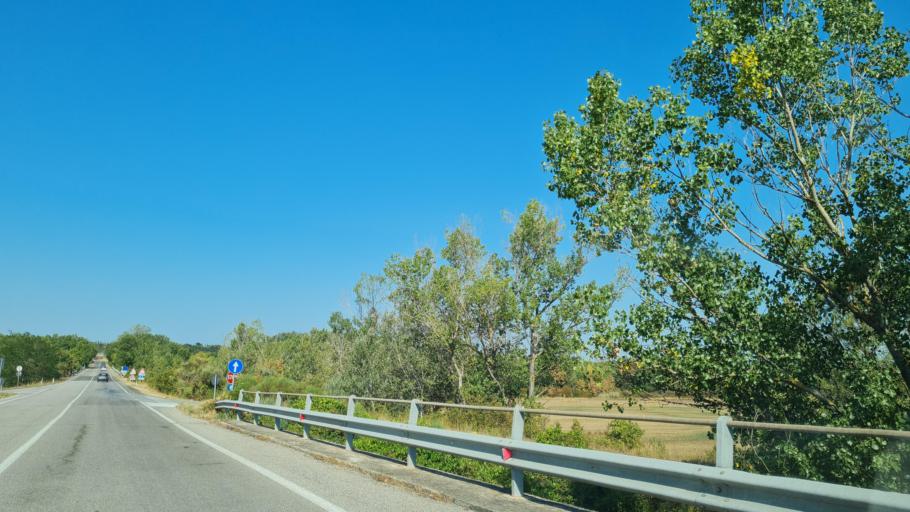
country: IT
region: Tuscany
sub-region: Provincia di Siena
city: Chianciano Terme
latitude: 43.0073
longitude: 11.7432
